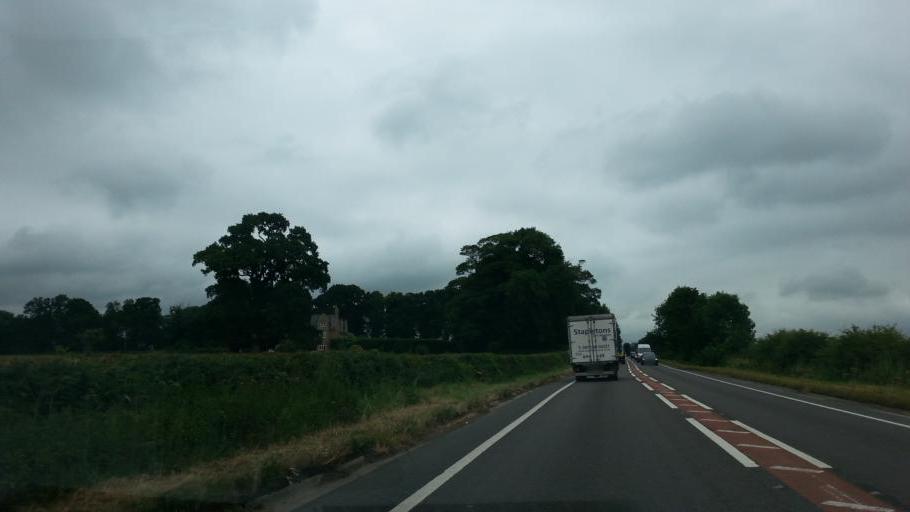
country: GB
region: England
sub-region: Northamptonshire
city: Northampton
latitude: 52.2994
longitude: -0.8283
